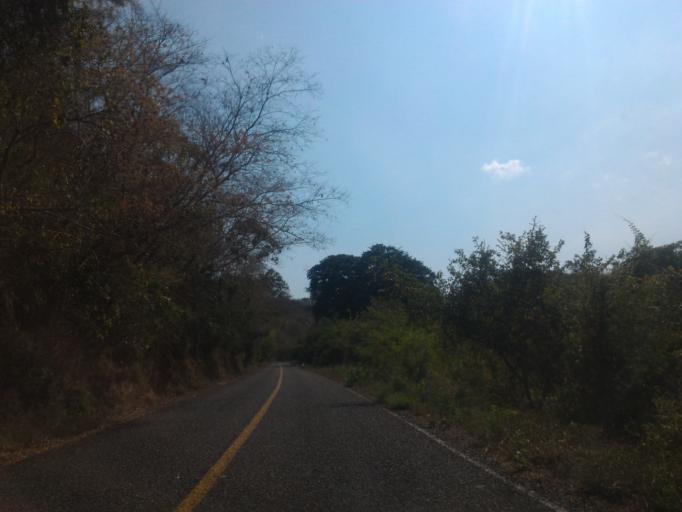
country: MX
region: Michoacan
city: Coahuayana Viejo
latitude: 18.3549
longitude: -103.4934
